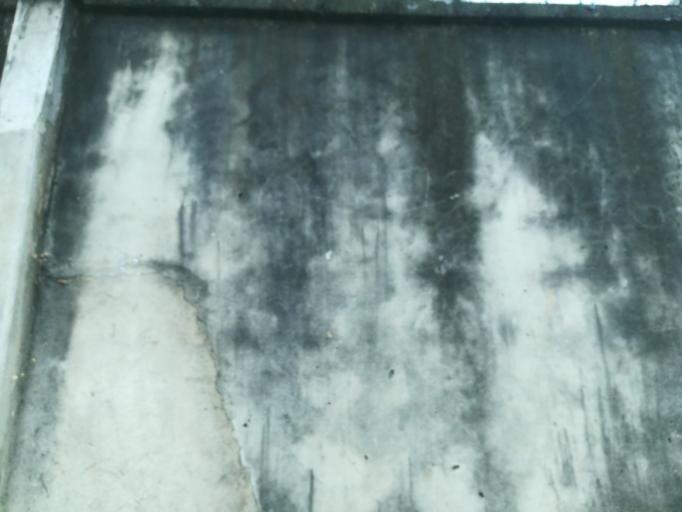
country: NG
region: Rivers
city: Port Harcourt
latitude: 4.8219
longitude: 7.0635
